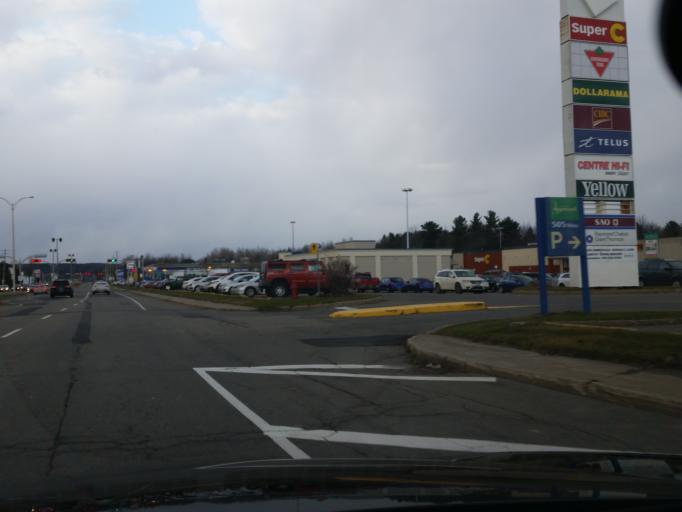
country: CA
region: Quebec
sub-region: Laurentides
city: Lachute
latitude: 45.6378
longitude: -74.3272
